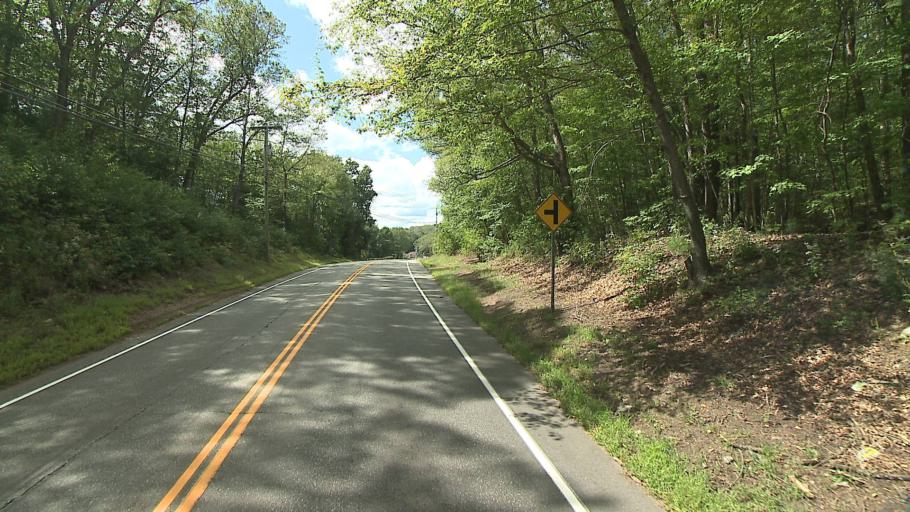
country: US
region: Connecticut
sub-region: Tolland County
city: Storrs
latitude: 41.8578
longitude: -72.1746
